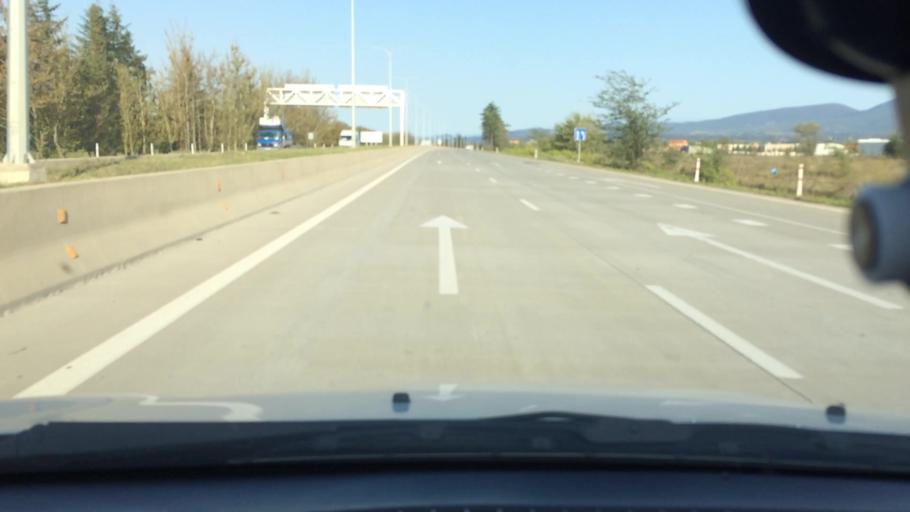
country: GE
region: Imereti
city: Zestap'oni
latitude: 42.1615
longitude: 42.9462
